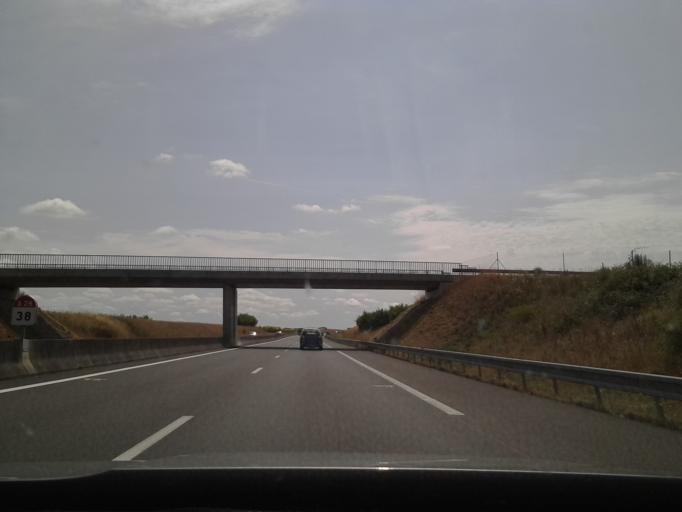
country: FR
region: Centre
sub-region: Departement d'Indre-et-Loire
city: Neuvy-le-Roi
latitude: 47.5787
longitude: 0.5754
